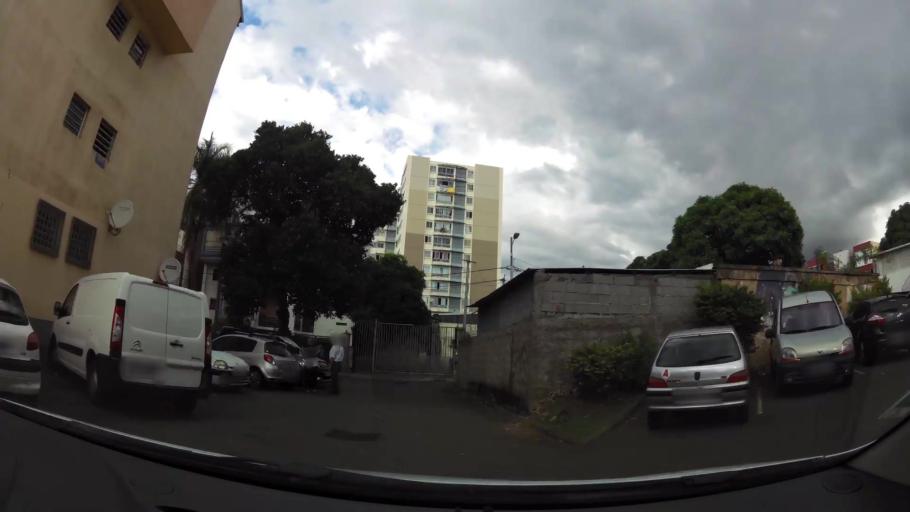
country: RE
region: Reunion
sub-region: Reunion
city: Saint-Denis
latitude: -20.8843
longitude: 55.4632
